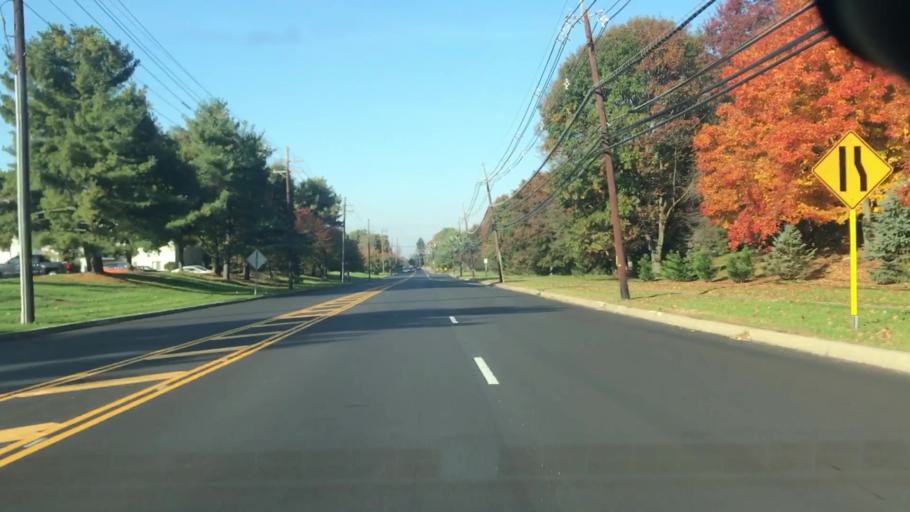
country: US
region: New Jersey
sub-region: Middlesex County
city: Princeton Meadows
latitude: 40.3370
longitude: -74.5599
